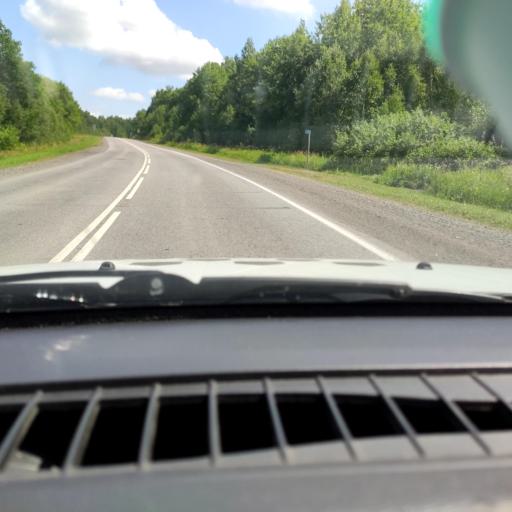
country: RU
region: Bashkortostan
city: Verkhniye Kigi
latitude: 55.3860
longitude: 58.6683
